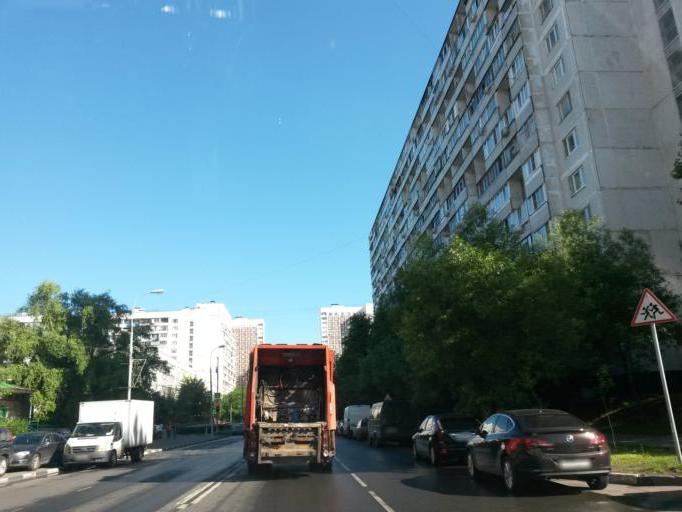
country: RU
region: Moscow
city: Brateyevo
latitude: 55.6400
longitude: 37.7707
